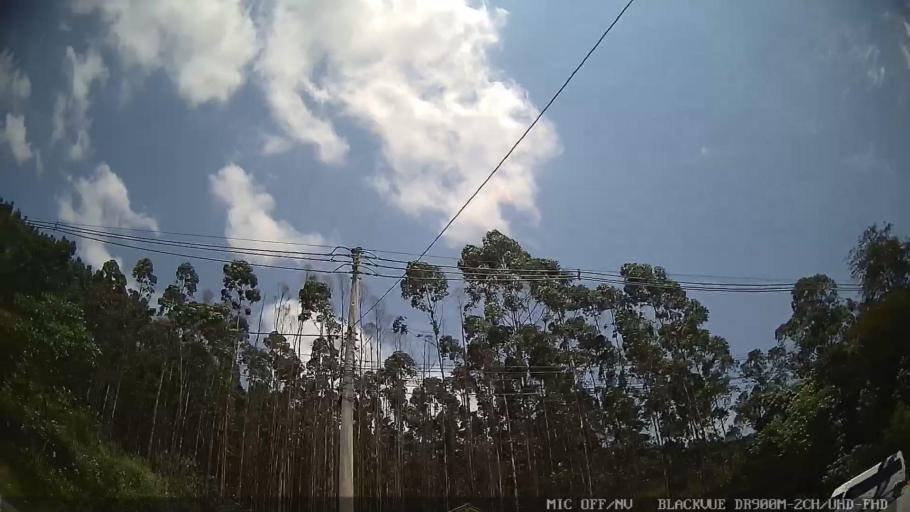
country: BR
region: Sao Paulo
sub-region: Caieiras
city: Caieiras
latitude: -23.3585
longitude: -46.7486
